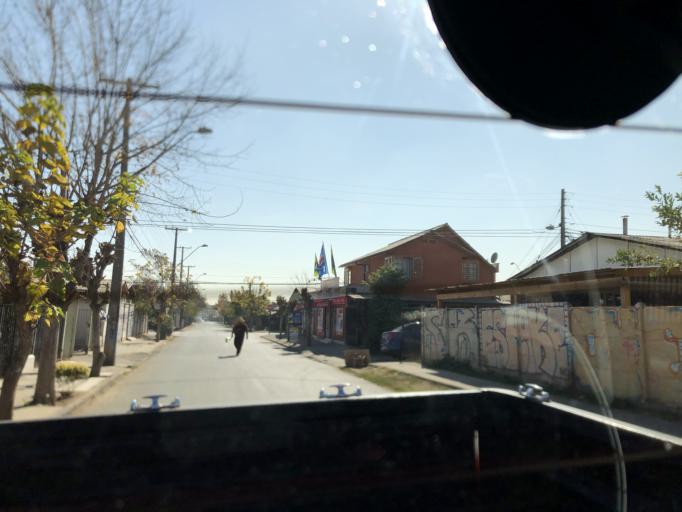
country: CL
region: Santiago Metropolitan
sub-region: Provincia de Cordillera
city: Puente Alto
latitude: -33.5648
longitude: -70.5698
